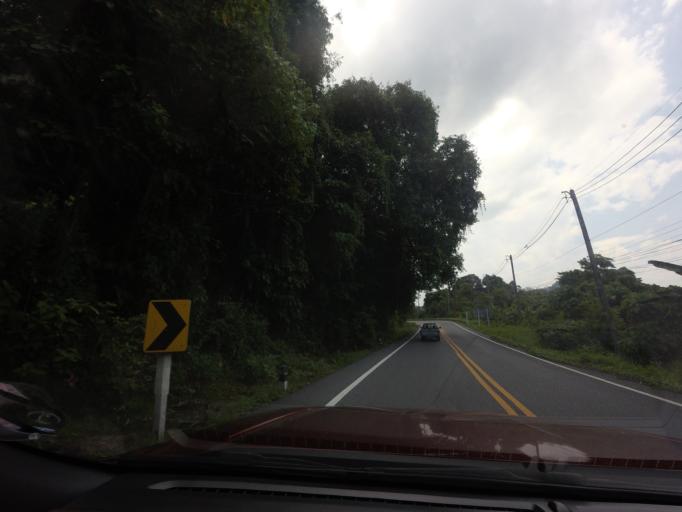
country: TH
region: Yala
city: Than To
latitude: 6.0376
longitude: 101.2009
